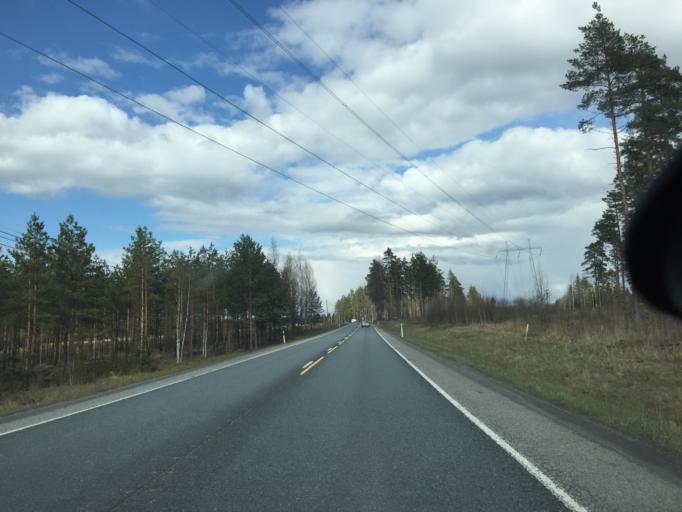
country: FI
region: Uusimaa
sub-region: Raaseporin
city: Inga
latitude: 60.1473
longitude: 23.8962
